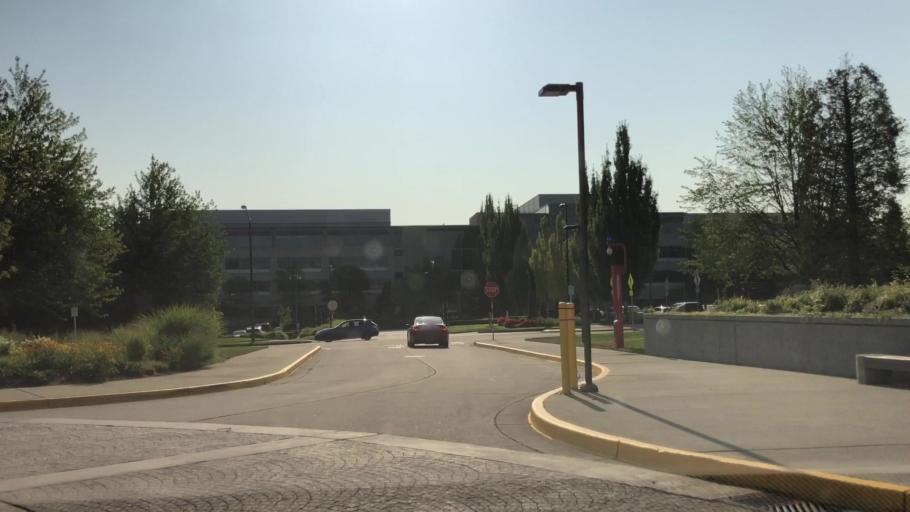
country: US
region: Washington
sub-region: King County
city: Redmond
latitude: 47.6442
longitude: -122.1280
